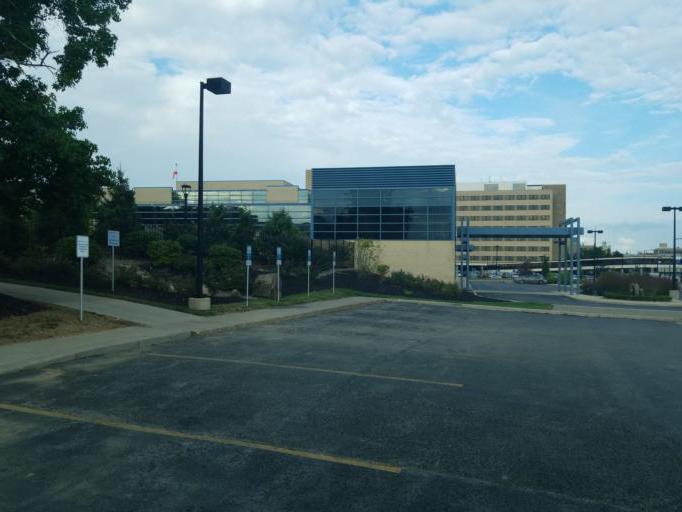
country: US
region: Ohio
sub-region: Mahoning County
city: Youngstown
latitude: 41.1135
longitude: -80.6595
